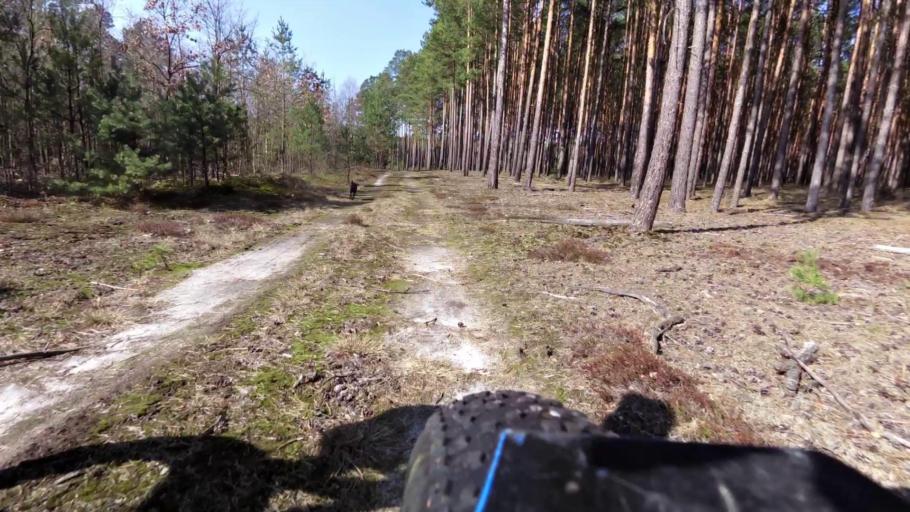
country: PL
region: Lubusz
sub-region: Powiat slubicki
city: Cybinka
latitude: 52.2106
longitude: 14.9147
